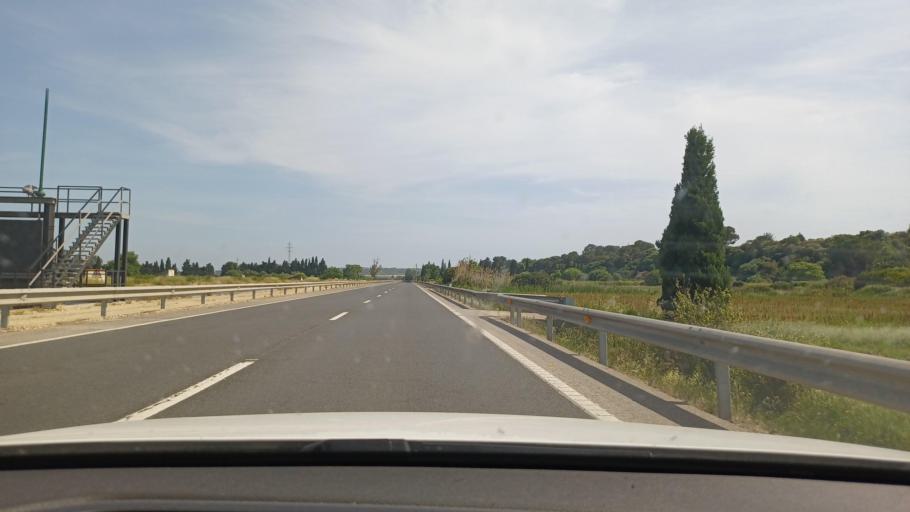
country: ES
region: Catalonia
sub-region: Provincia de Tarragona
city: Tortosa
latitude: 40.7700
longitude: 0.5299
